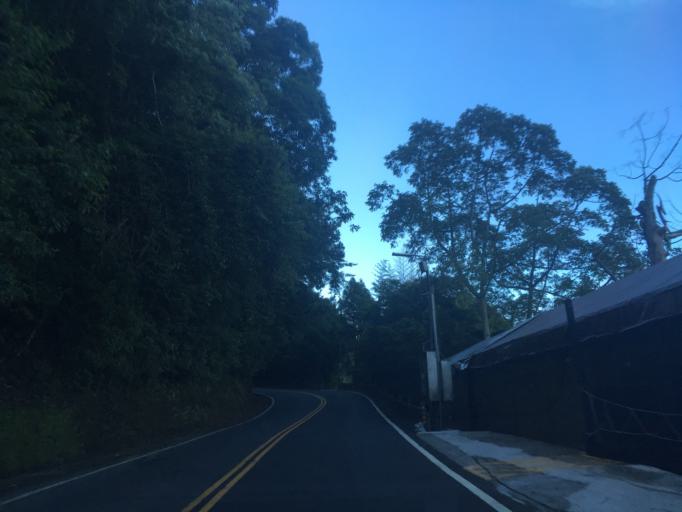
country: TW
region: Taiwan
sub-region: Nantou
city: Puli
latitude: 24.0368
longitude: 121.1469
